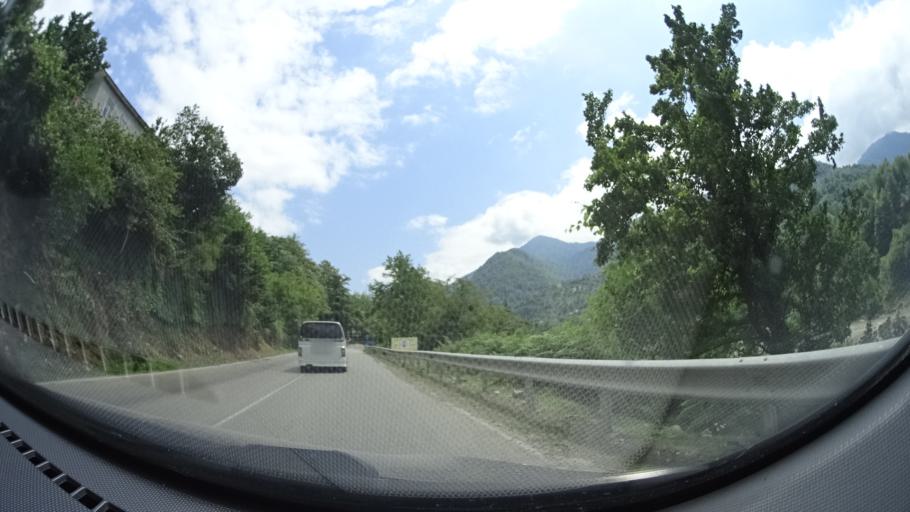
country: TR
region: Artvin
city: Camili
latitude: 41.5657
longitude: 41.8286
